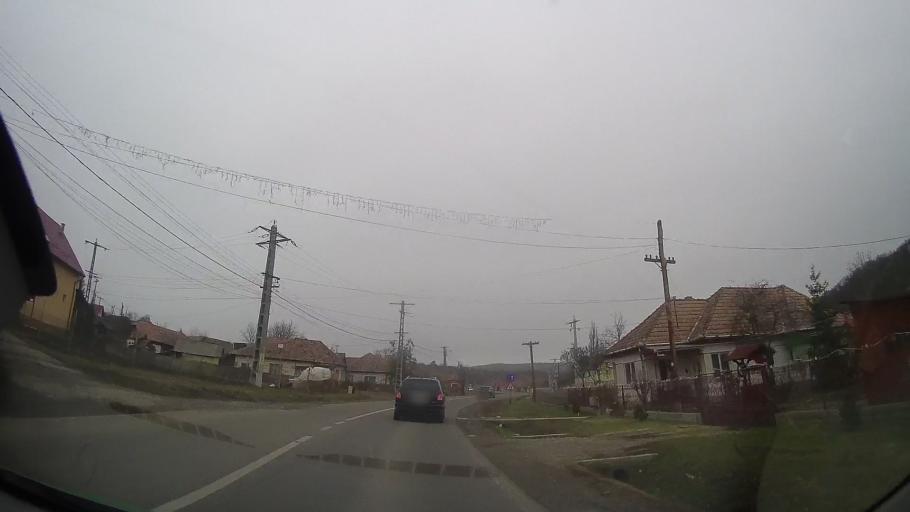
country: RO
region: Mures
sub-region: Comuna Ceausu de Campie
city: Ceausu de Campie
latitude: 46.6366
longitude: 24.5168
